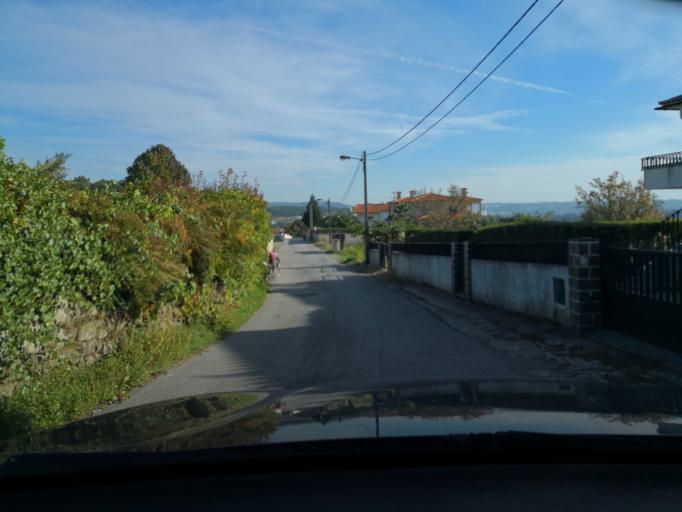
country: PT
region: Vila Real
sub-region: Vila Real
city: Vila Real
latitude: 41.3321
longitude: -7.7428
